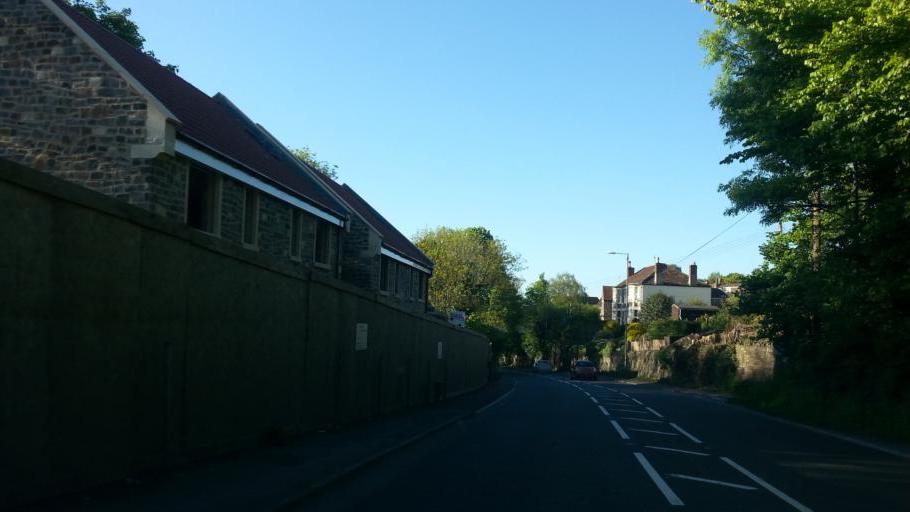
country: GB
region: England
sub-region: Bath and North East Somerset
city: Publow
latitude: 51.3691
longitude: -2.5476
